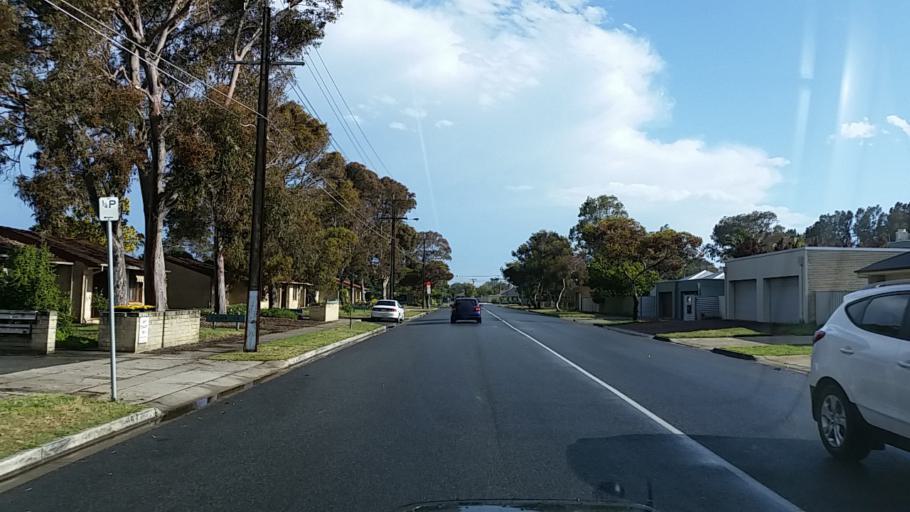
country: AU
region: South Australia
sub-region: Charles Sturt
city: Henley Beach
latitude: -34.9115
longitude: 138.4994
